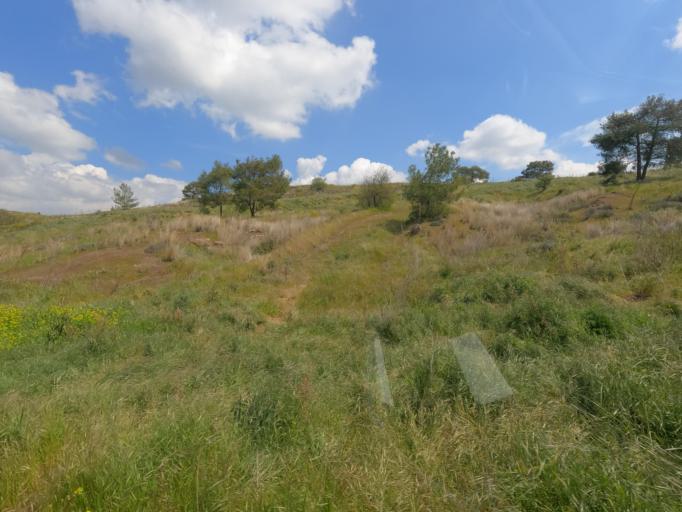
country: CY
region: Lefkosia
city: Lefka
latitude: 35.0784
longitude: 32.9414
